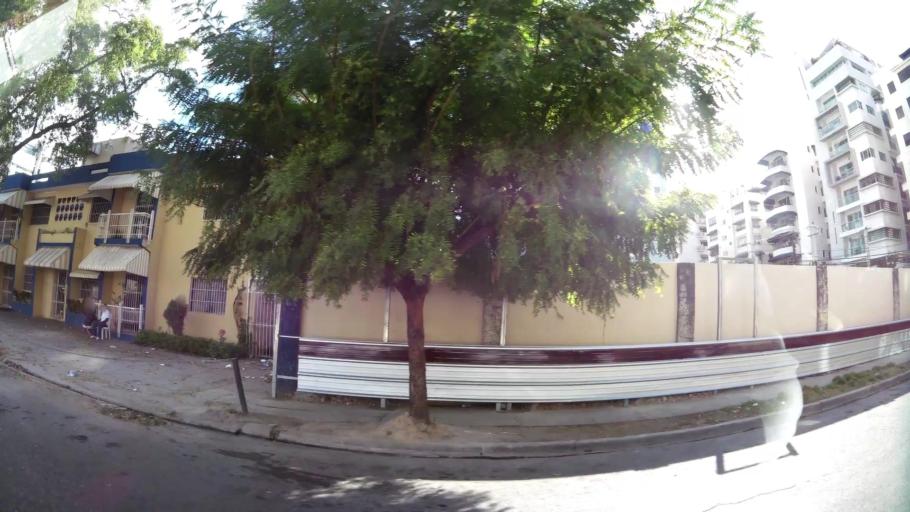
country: DO
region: Nacional
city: La Julia
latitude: 18.4791
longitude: -69.9424
